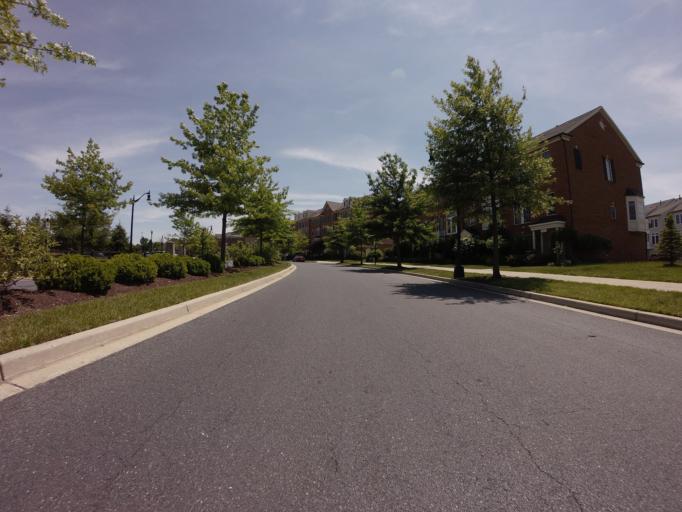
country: US
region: Maryland
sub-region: Frederick County
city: Urbana
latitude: 39.3355
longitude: -77.3358
